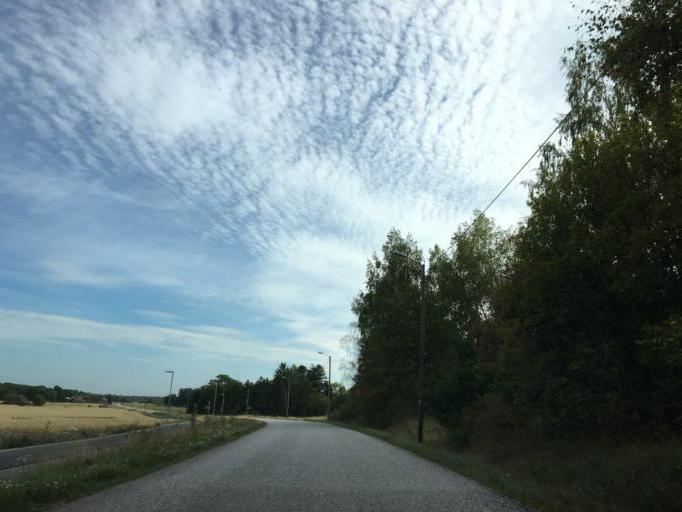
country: SE
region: Soedermanland
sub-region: Eskilstuna Kommun
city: Torshalla
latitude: 59.4465
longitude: 16.4688
